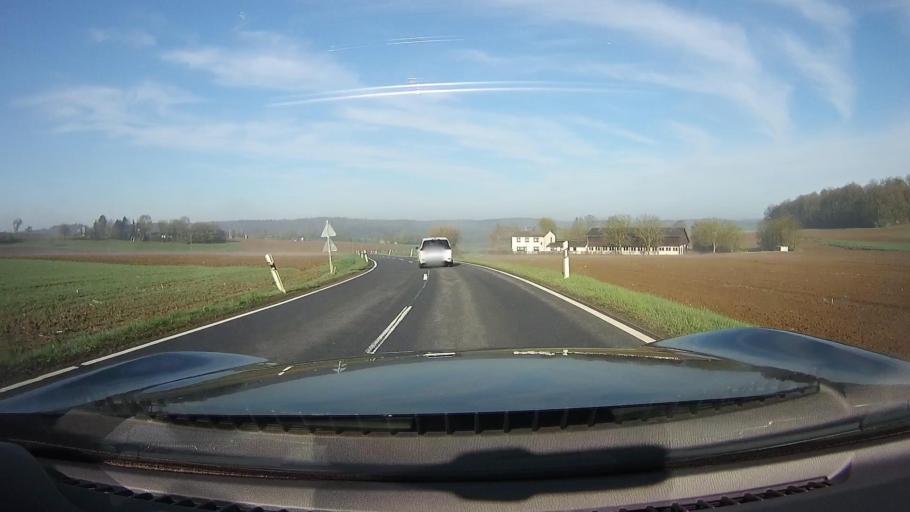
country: DE
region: Baden-Wuerttemberg
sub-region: Karlsruhe Region
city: Adelsheim
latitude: 49.4049
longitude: 9.3635
